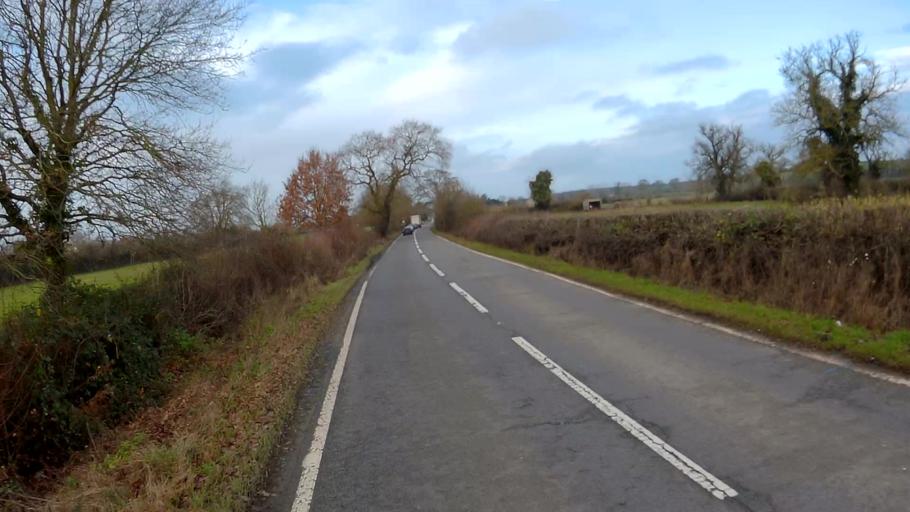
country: GB
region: England
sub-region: Lincolnshire
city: Bourne
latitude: 52.7771
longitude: -0.4261
